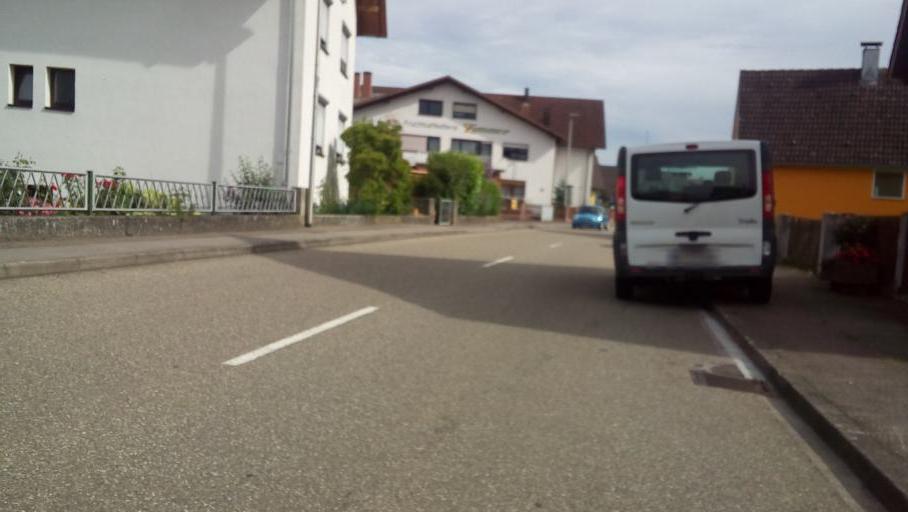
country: DE
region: Baden-Wuerttemberg
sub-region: Karlsruhe Region
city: Lichtenau
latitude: 48.7065
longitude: 7.9691
